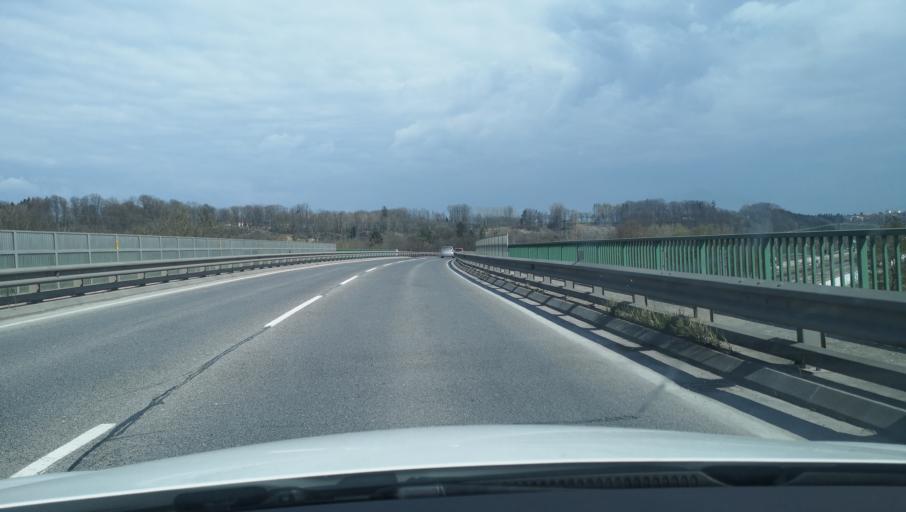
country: AT
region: Lower Austria
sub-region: Politischer Bezirk Amstetten
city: Winklarn
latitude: 48.1107
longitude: 14.8376
